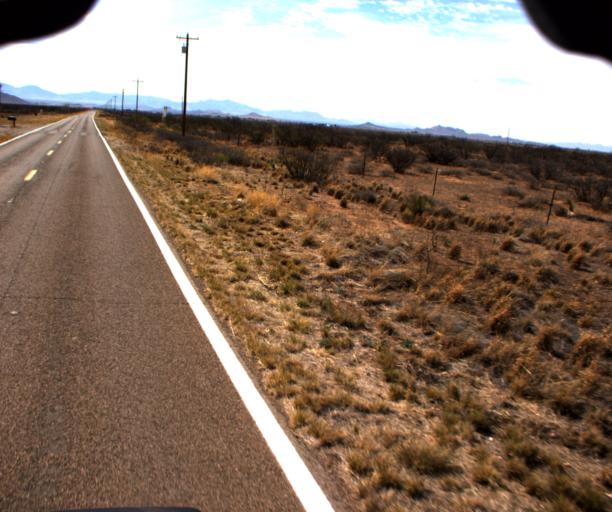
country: US
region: Arizona
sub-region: Cochise County
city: Willcox
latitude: 31.8760
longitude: -109.5742
